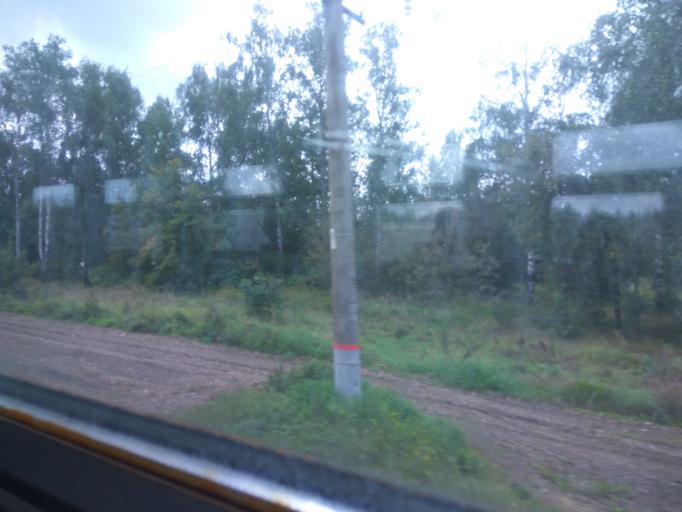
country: RU
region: Moskovskaya
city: Beloozerskiy
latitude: 55.4707
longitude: 38.4304
